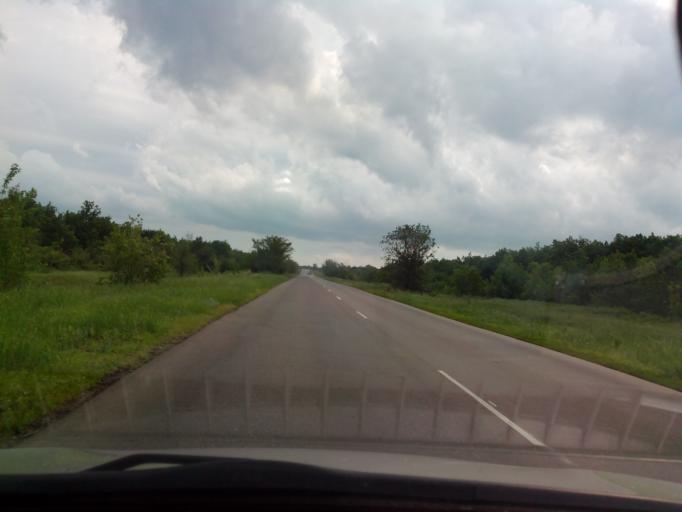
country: RU
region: Volgograd
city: Mikhaylovka
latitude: 49.9683
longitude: 43.0476
